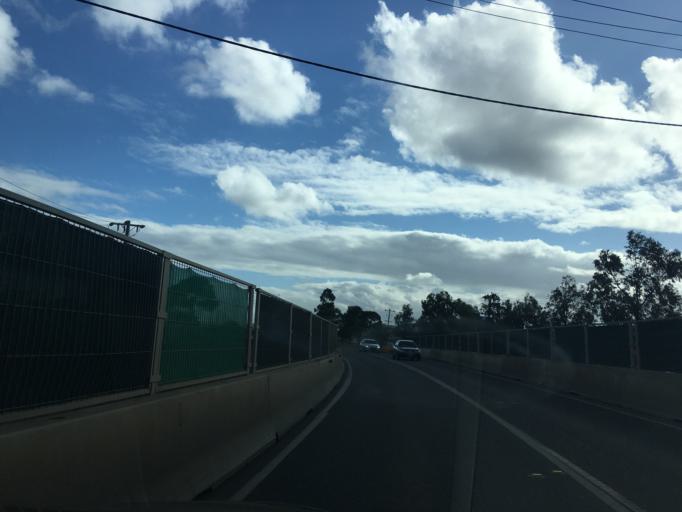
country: AU
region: Victoria
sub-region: Wyndham
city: Williams Landing
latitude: -37.8687
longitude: 144.7321
